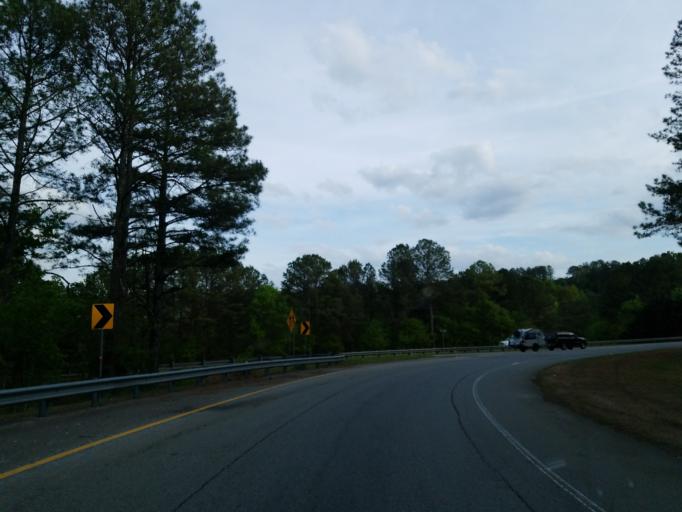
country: US
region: Georgia
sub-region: Cherokee County
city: Canton
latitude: 34.2248
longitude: -84.4838
